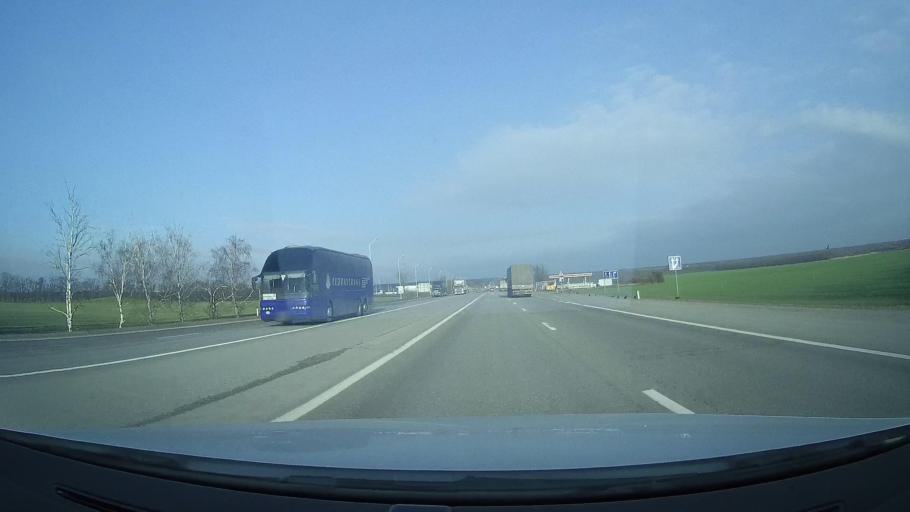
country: RU
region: Rostov
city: Grushevskaya
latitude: 47.4633
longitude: 39.9731
